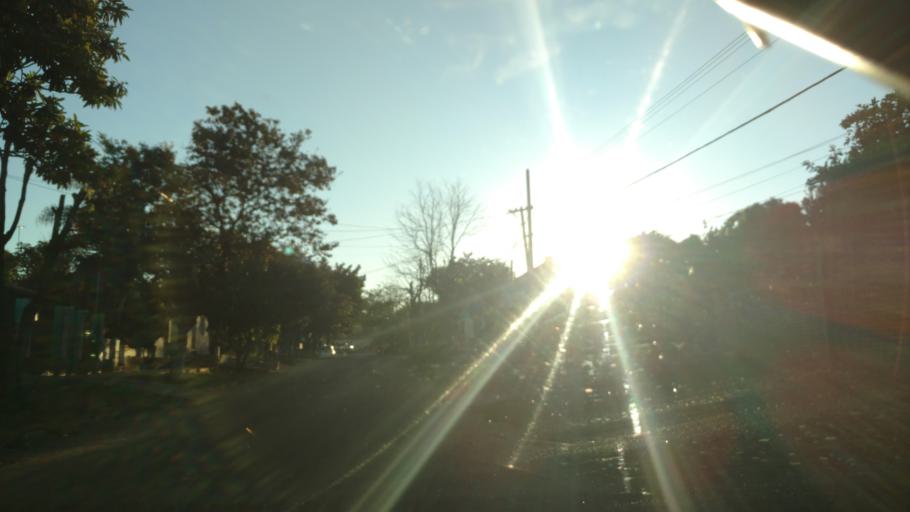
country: PY
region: Paraguari
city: Yaguaron
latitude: -25.5651
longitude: -57.2882
